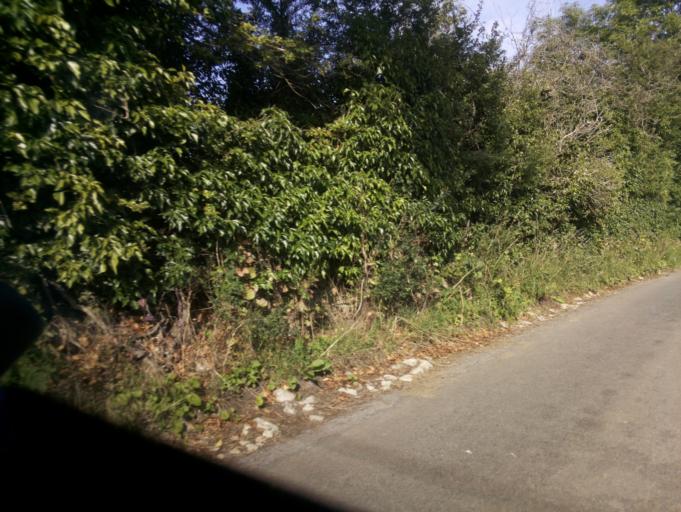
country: GB
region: England
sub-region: South Gloucestershire
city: Bitton
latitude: 51.4379
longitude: -2.4349
